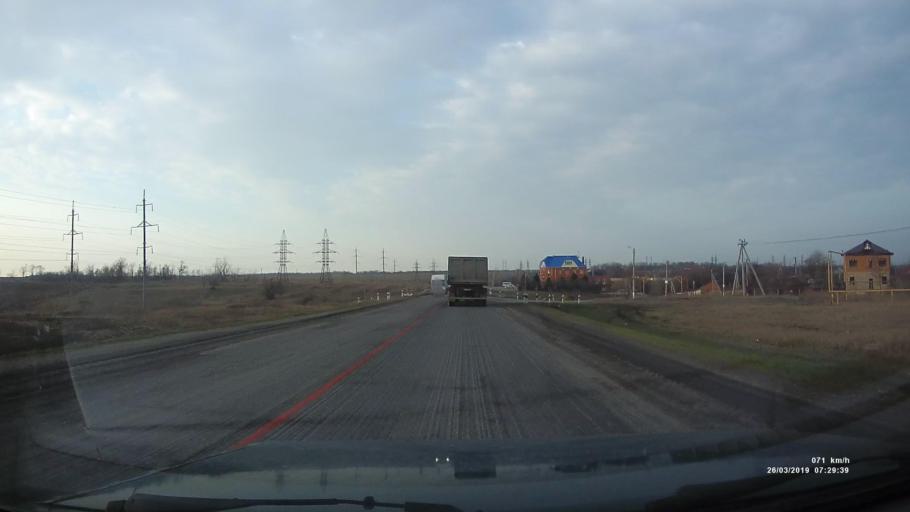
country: RU
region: Rostov
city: Novobessergenovka
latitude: 47.2432
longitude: 38.8150
